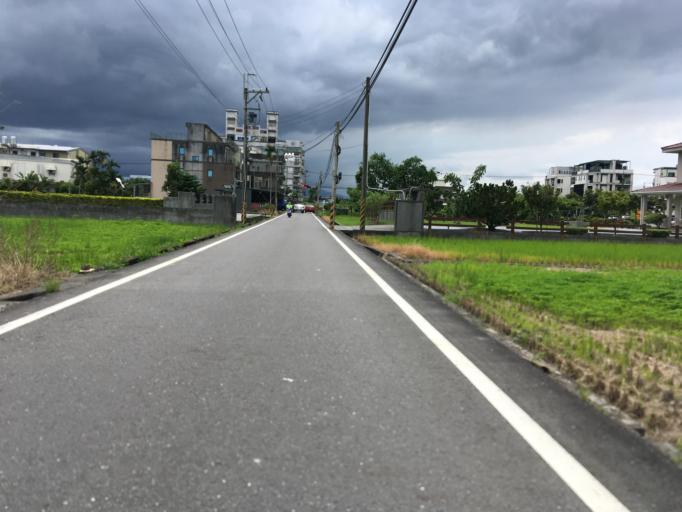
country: TW
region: Taiwan
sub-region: Yilan
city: Yilan
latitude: 24.6906
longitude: 121.7980
